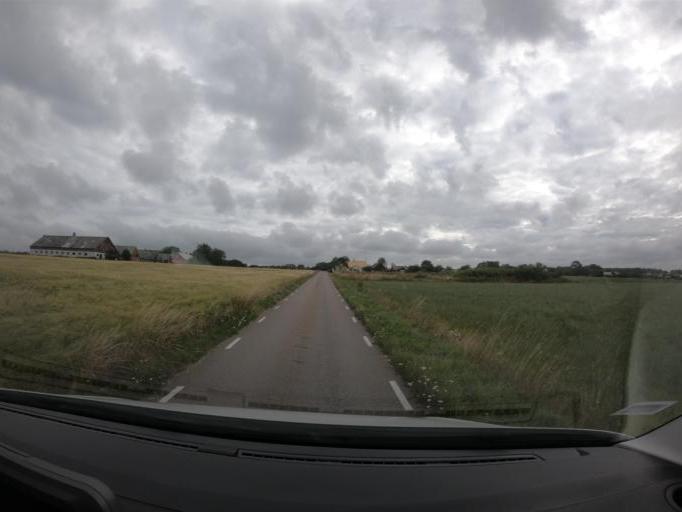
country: SE
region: Skane
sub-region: Bastads Kommun
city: Forslov
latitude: 56.3320
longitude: 12.8159
